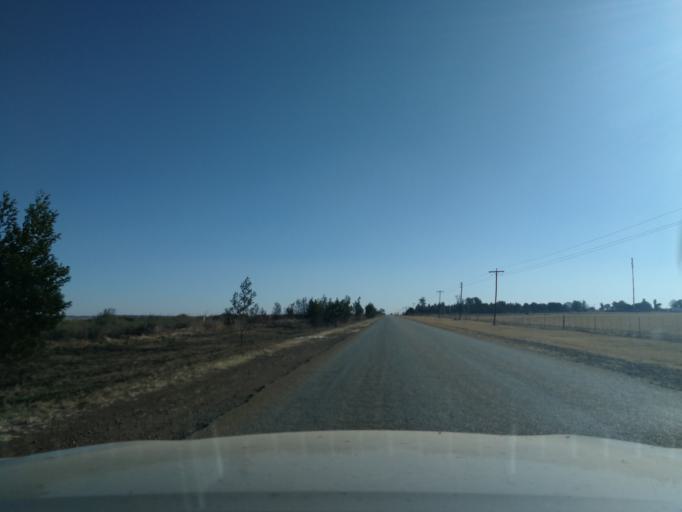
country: ZA
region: Gauteng
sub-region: West Rand District Municipality
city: Randfontein
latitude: -25.9911
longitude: 27.4144
